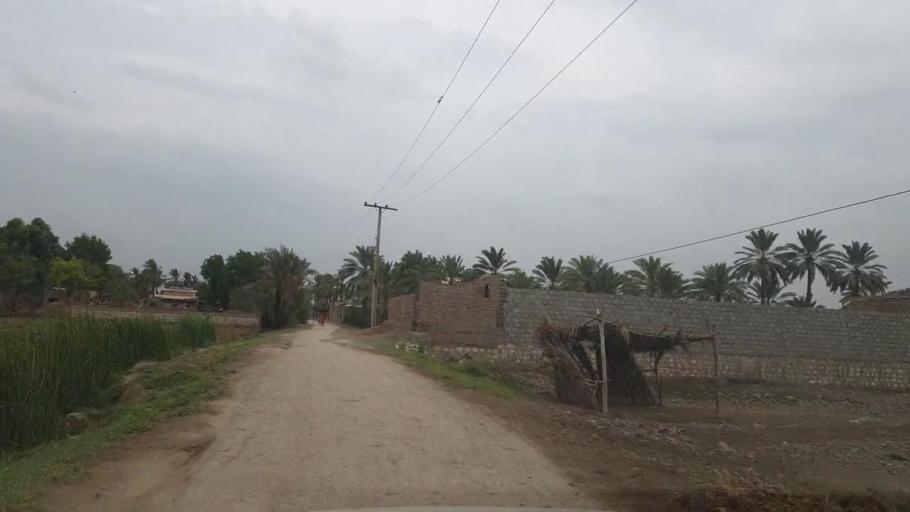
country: PK
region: Sindh
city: Khairpur
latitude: 27.5464
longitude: 68.7395
